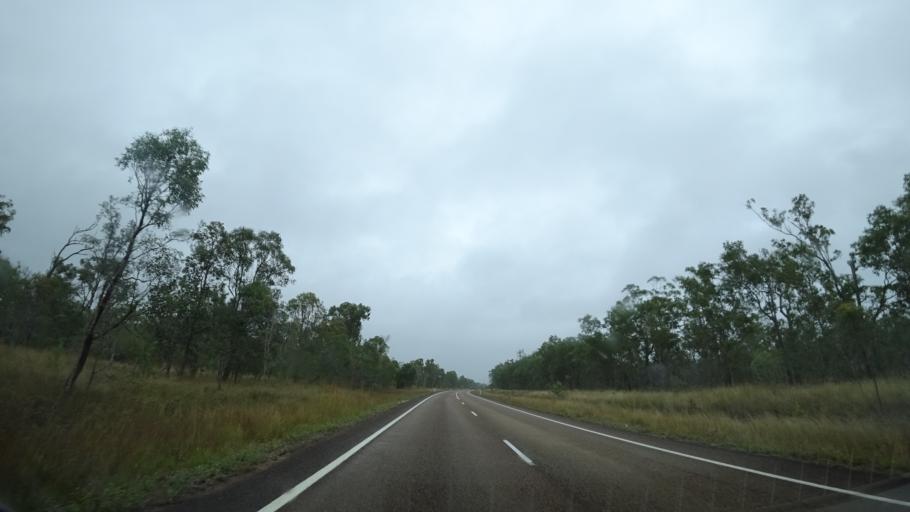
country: AU
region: Queensland
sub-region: Tablelands
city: Ravenshoe
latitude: -17.6920
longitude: 145.2221
